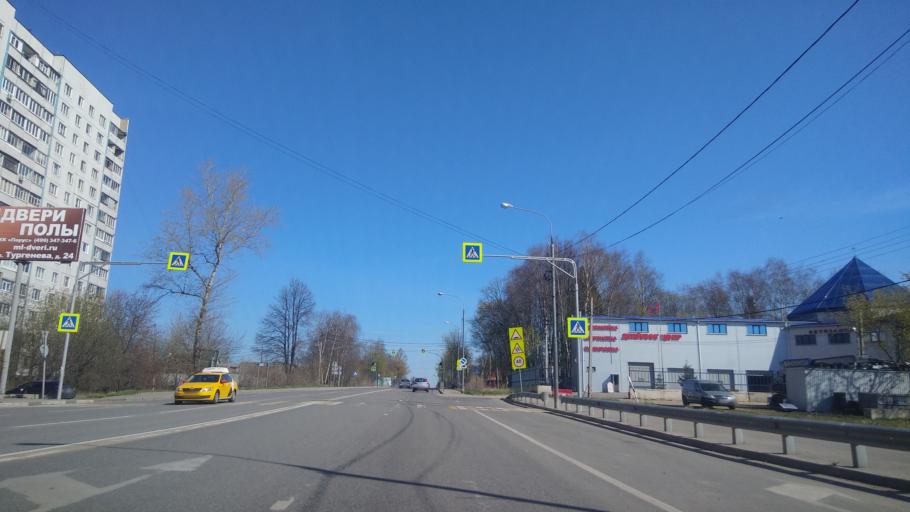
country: RU
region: Moskovskaya
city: Pushkino
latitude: 56.0134
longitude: 37.8721
